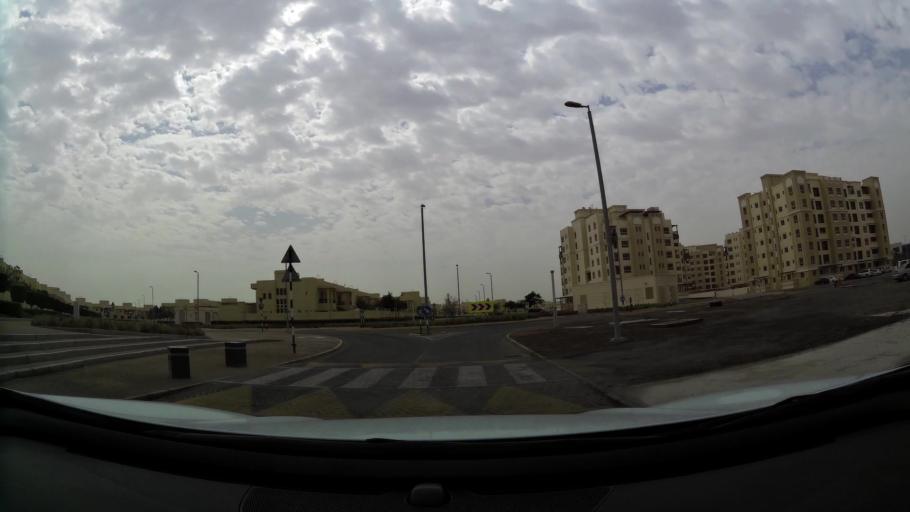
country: AE
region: Abu Dhabi
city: Abu Dhabi
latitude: 24.3126
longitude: 54.6241
